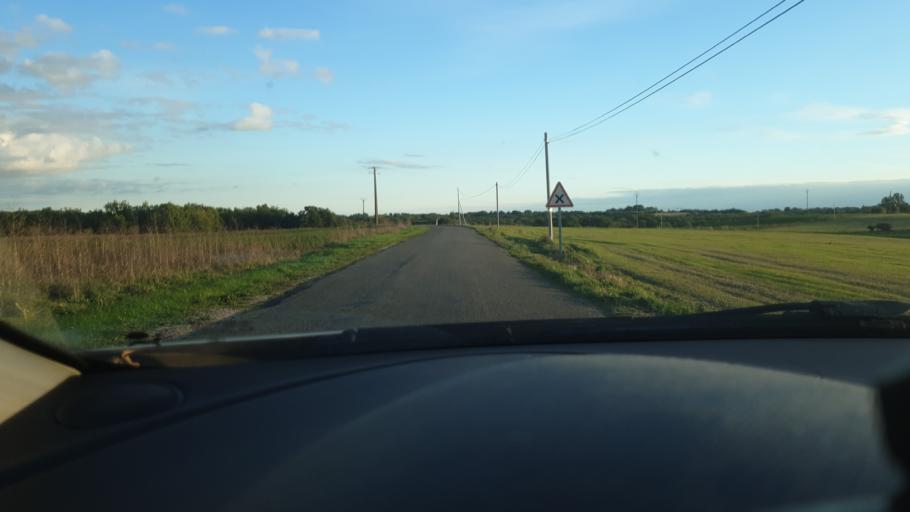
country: FR
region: Midi-Pyrenees
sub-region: Departement du Lot
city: Montcuq
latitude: 44.3997
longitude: 1.2199
